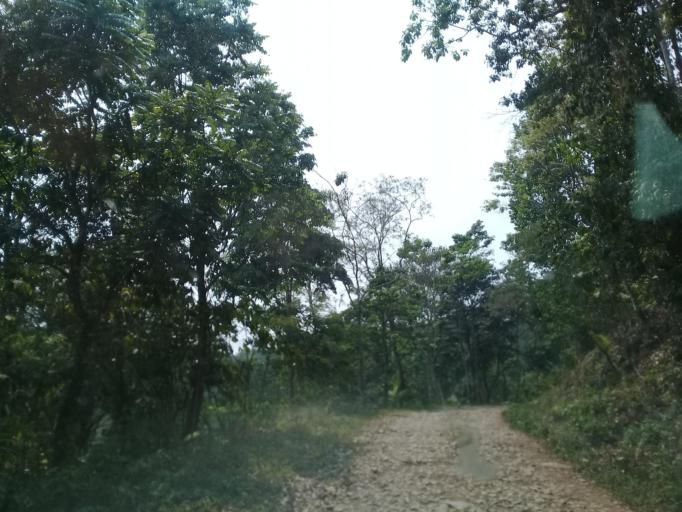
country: MX
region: Veracruz
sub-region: Tezonapa
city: Laguna Chica (Pueblo Nuevo)
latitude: 18.5796
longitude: -96.7531
